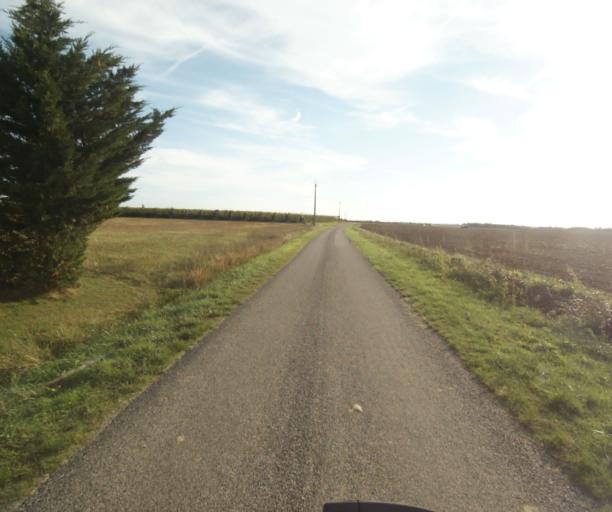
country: FR
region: Midi-Pyrenees
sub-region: Departement du Tarn-et-Garonne
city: Finhan
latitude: 43.9202
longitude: 1.1340
